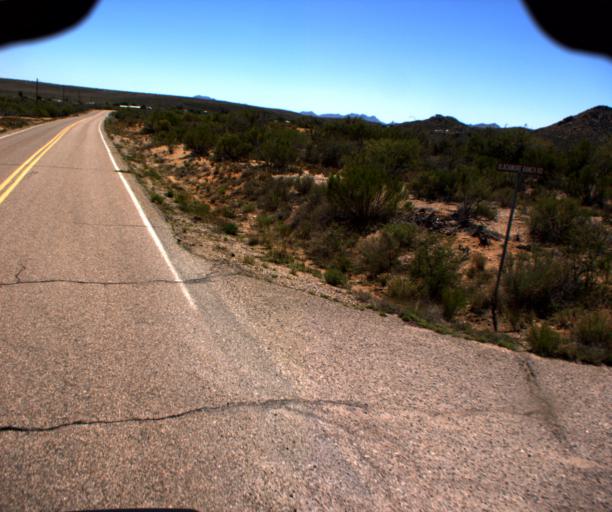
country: US
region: Arizona
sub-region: Yavapai County
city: Congress
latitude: 34.4296
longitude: -112.9168
